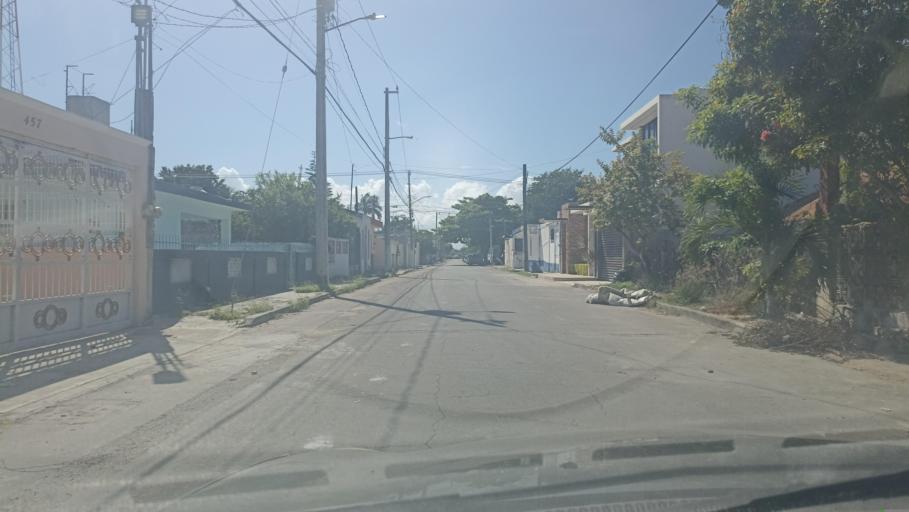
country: MX
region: Quintana Roo
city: Chetumal
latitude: 18.5156
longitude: -88.2856
